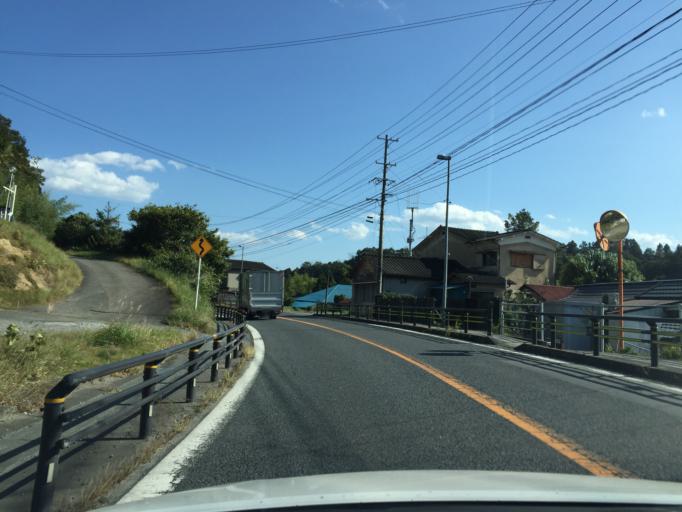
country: JP
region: Fukushima
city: Iwaki
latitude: 37.0715
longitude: 140.8293
